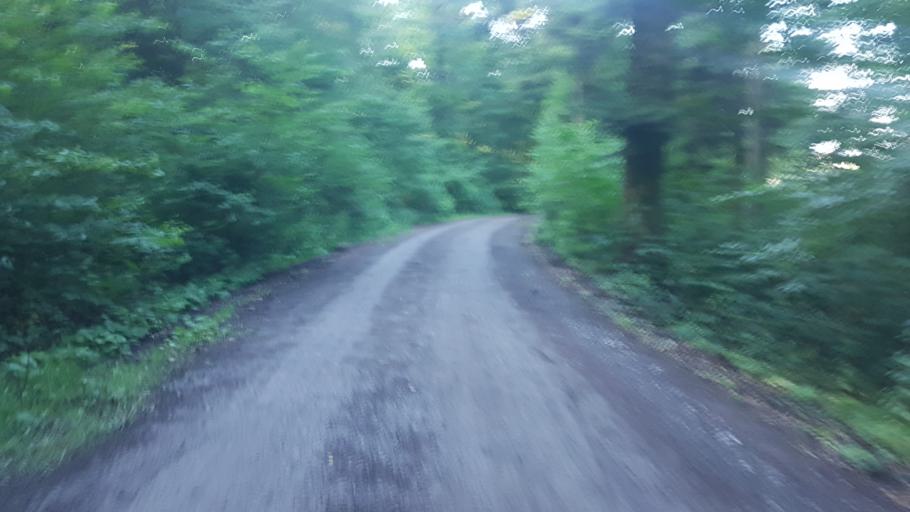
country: DE
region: Baden-Wuerttemberg
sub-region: Karlsruhe Region
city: Sternenfels
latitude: 49.0522
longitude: 8.8802
